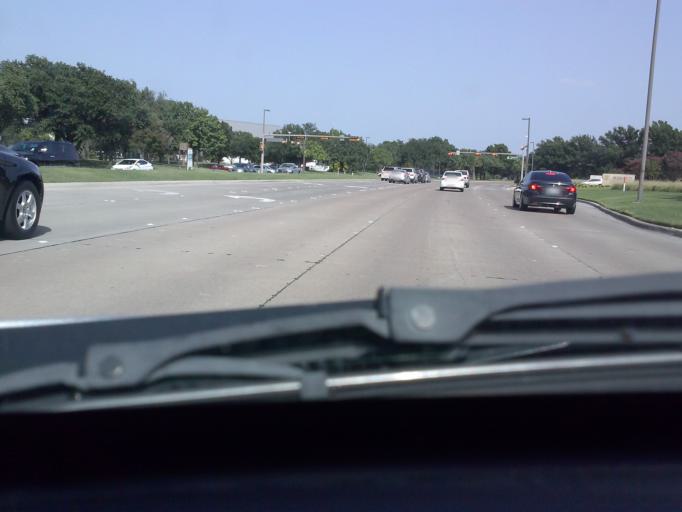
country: US
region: Texas
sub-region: Collin County
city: Frisco
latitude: 33.0772
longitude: -96.8089
